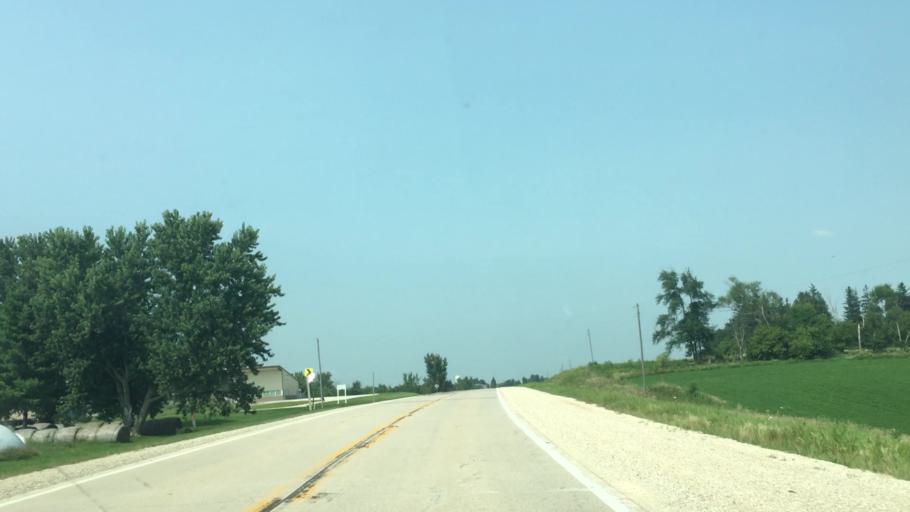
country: US
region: Iowa
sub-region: Winneshiek County
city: Decorah
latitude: 43.1642
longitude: -91.8644
